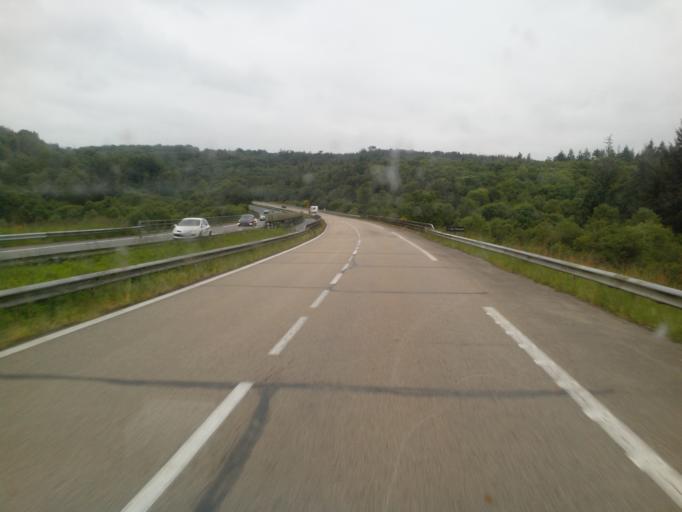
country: FR
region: Brittany
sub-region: Departement du Finistere
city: Plouigneau
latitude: 48.5776
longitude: -3.6428
